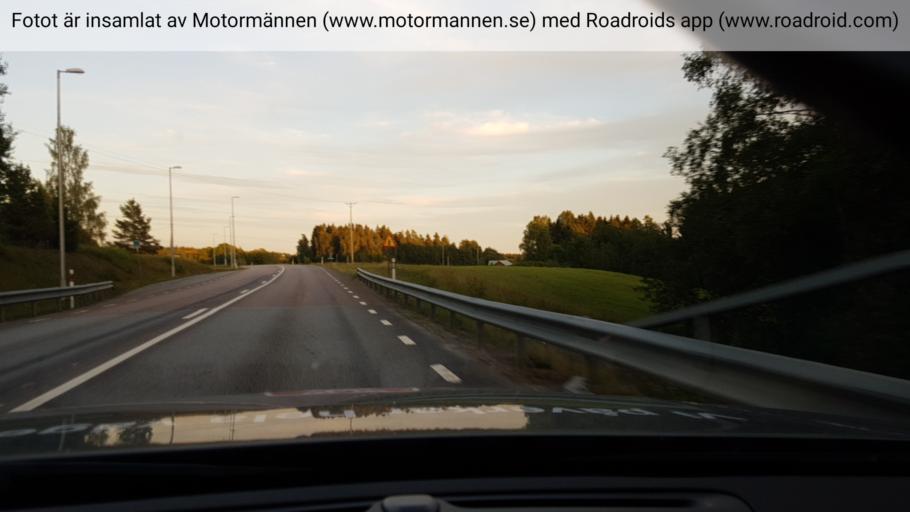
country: SE
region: OErebro
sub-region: Karlskoga Kommun
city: Karlskoga
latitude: 59.3873
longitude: 14.4736
